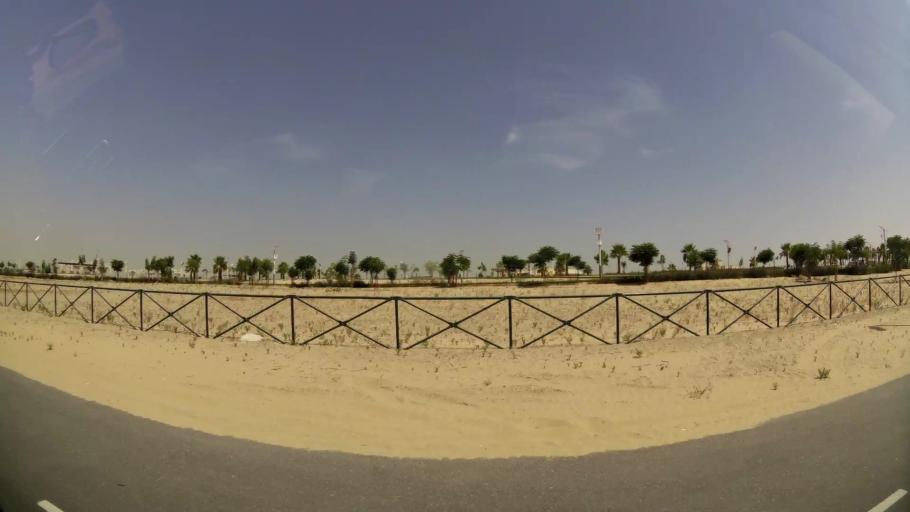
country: AE
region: Ash Shariqah
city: Sharjah
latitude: 25.1893
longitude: 55.4225
